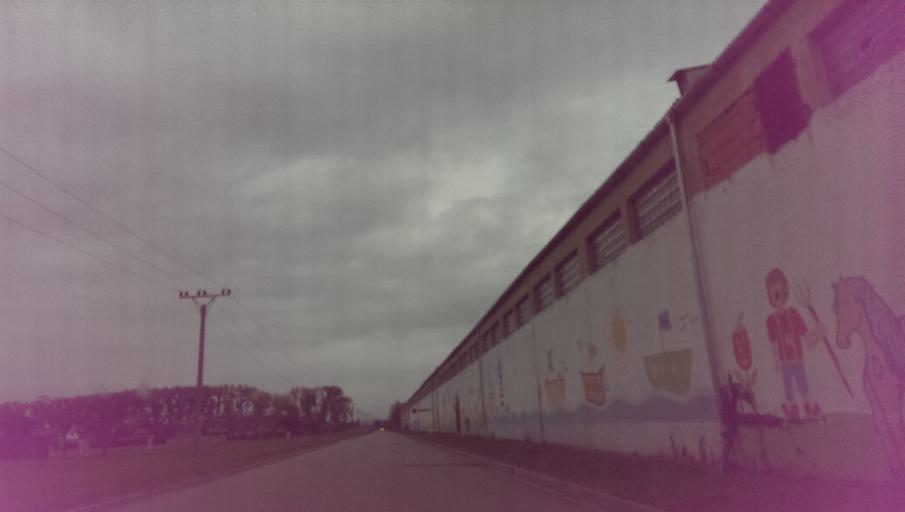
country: CZ
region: South Moravian
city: Pohorelice
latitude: 48.9820
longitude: 16.5133
